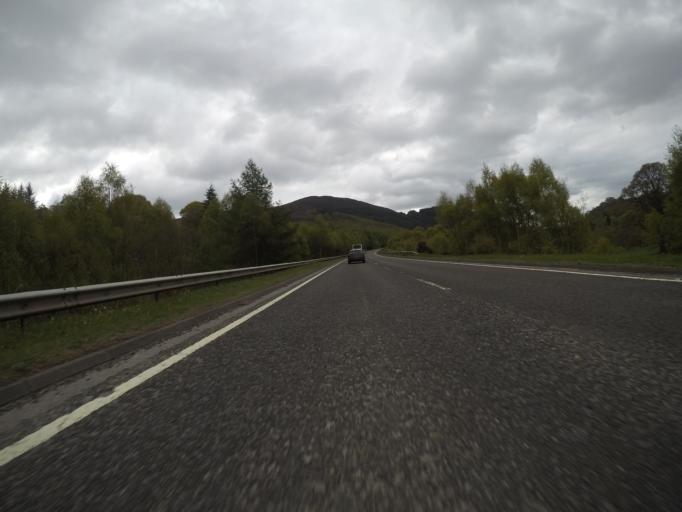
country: GB
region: Scotland
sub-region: Perth and Kinross
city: Pitlochry
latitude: 56.7459
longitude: -3.7730
